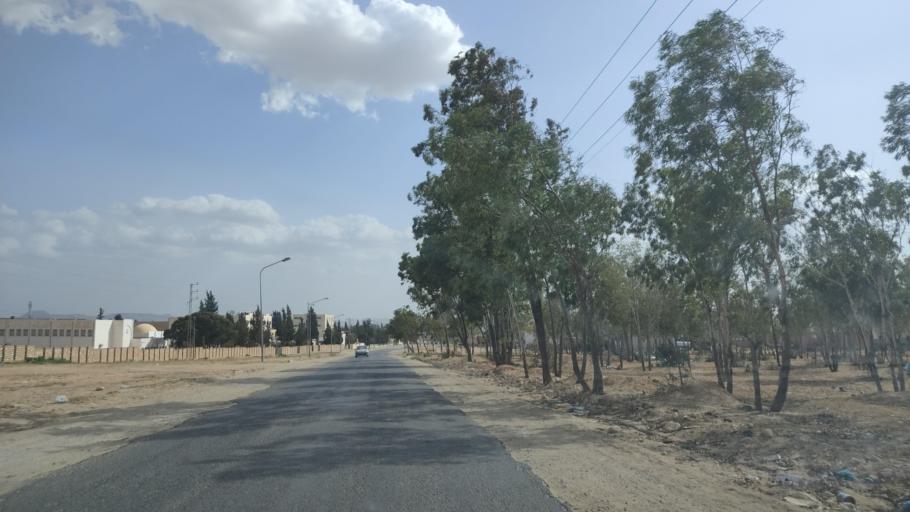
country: TN
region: Sidi Bu Zayd
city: Sidi Bouzid
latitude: 35.1074
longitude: 9.5384
